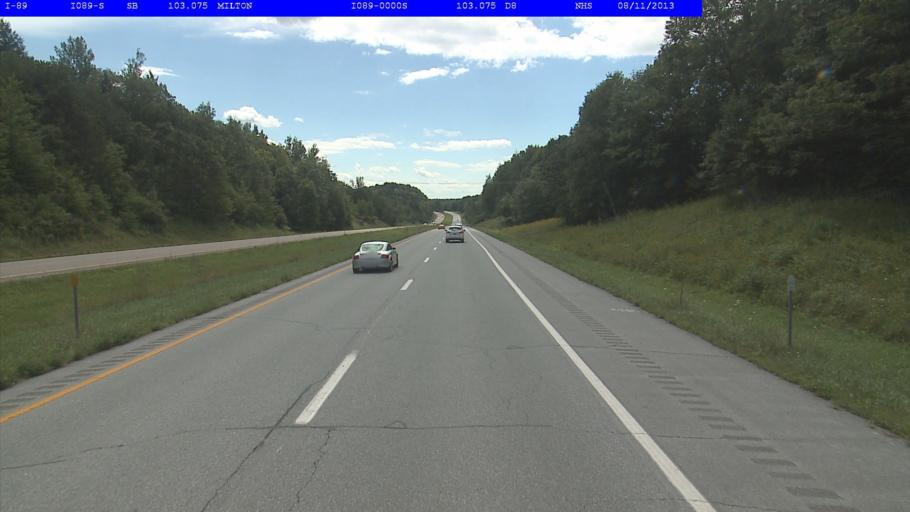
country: US
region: Vermont
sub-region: Chittenden County
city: Milton
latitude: 44.6579
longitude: -73.1387
